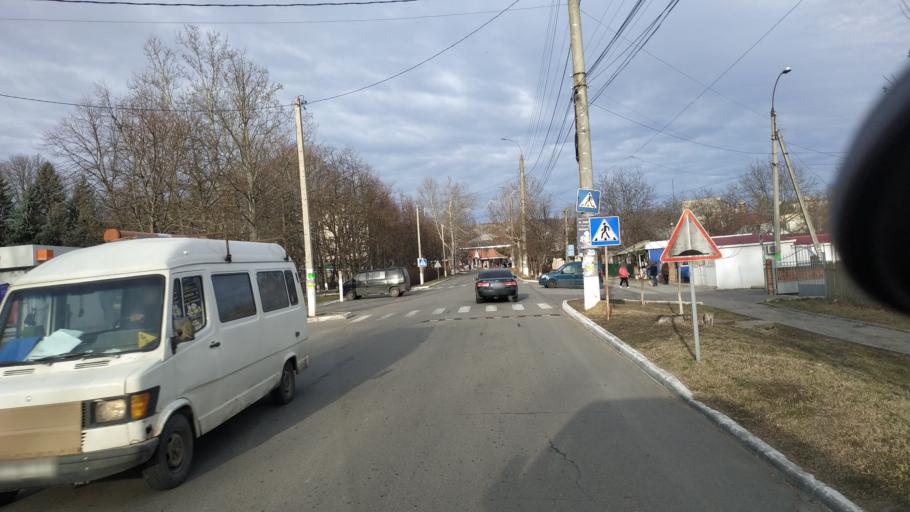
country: MD
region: Chisinau
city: Vadul lui Voda
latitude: 47.0870
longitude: 29.0821
